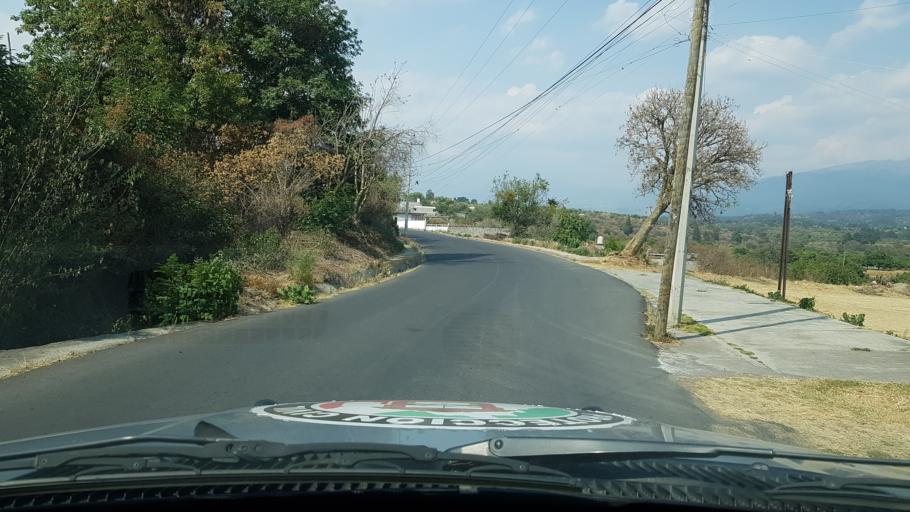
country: MX
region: Mexico
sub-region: Atlautla
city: San Andres Tlalamac
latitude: 18.9747
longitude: -98.8144
